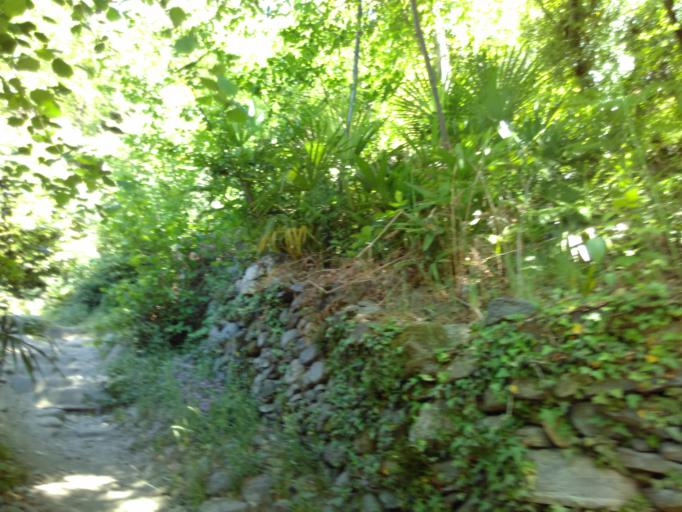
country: CH
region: Ticino
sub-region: Bellinzona District
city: Sementina
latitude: 46.1874
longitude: 8.9859
